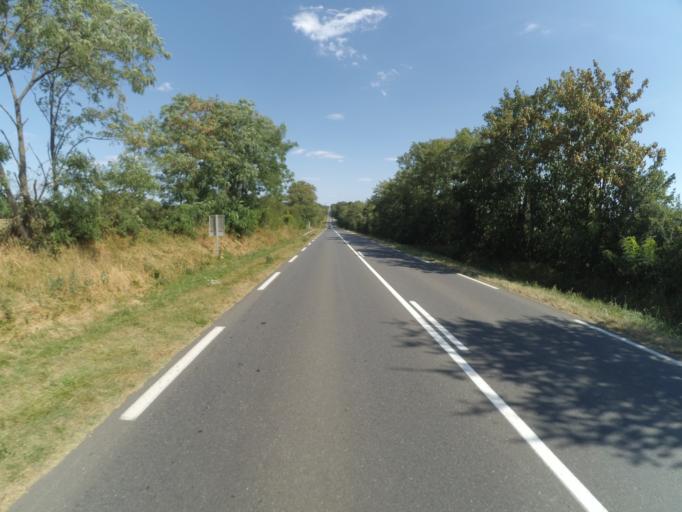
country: FR
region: Poitou-Charentes
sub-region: Departement de la Vienne
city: Terce
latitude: 46.4310
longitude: 0.6103
